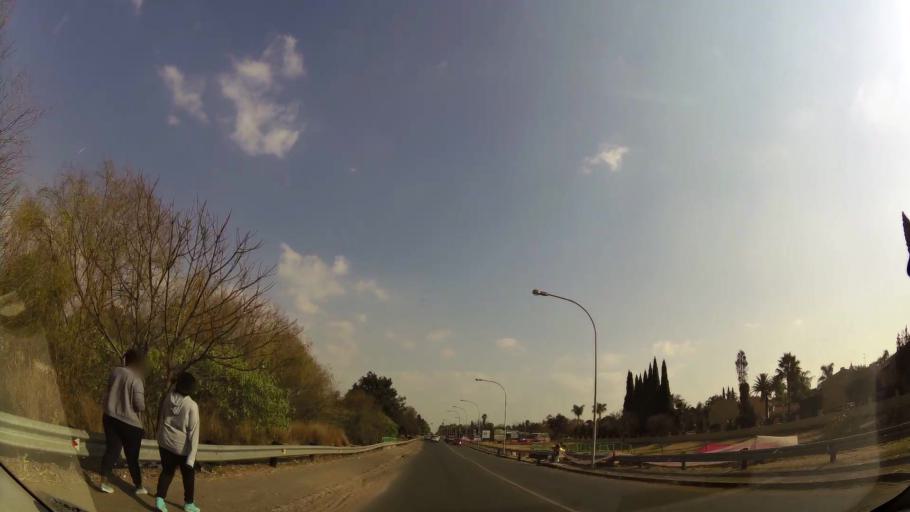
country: ZA
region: Gauteng
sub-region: Ekurhuleni Metropolitan Municipality
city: Benoni
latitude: -26.1595
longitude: 28.2872
